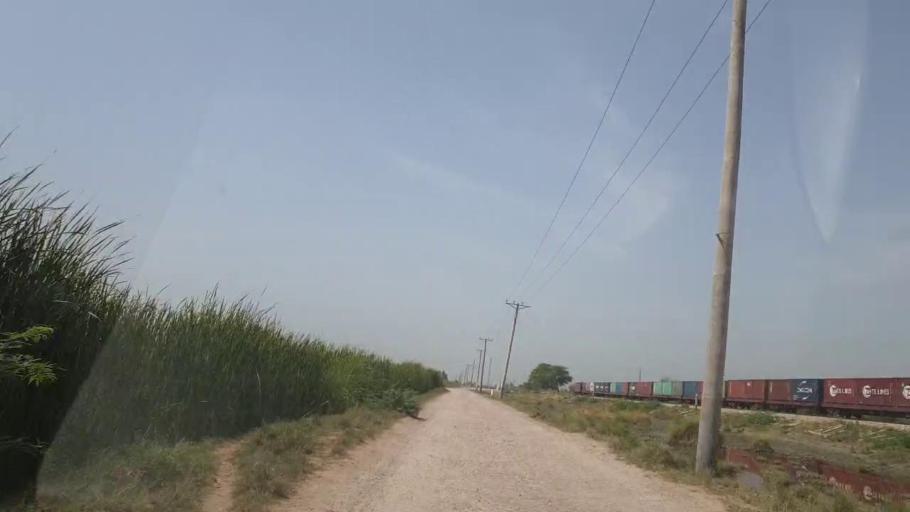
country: PK
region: Sindh
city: Gambat
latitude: 27.3264
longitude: 68.5392
